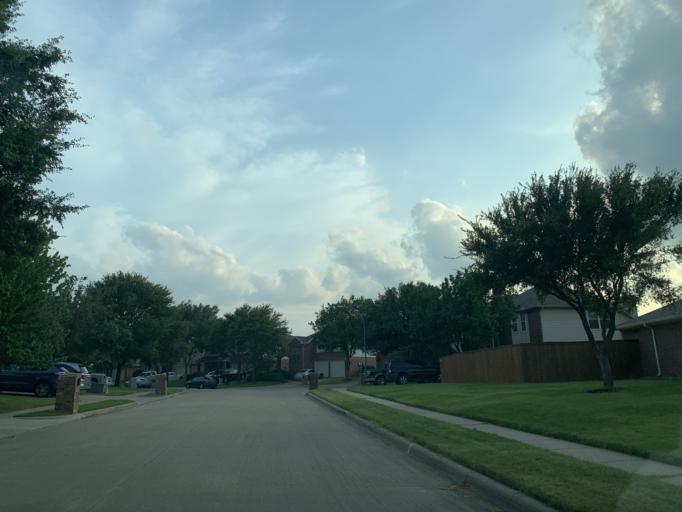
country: US
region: Texas
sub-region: Tarrant County
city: Keller
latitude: 32.9404
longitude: -97.2742
